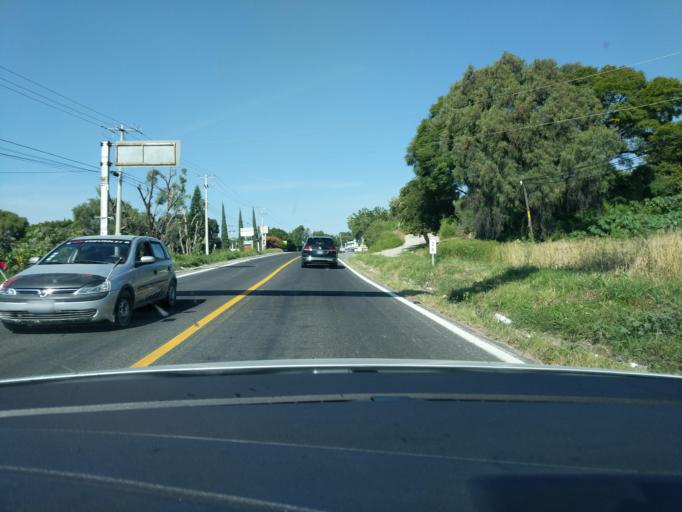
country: MX
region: Puebla
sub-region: Atlixco
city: San Agustin Huixaxtla
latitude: 18.9305
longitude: -98.4073
